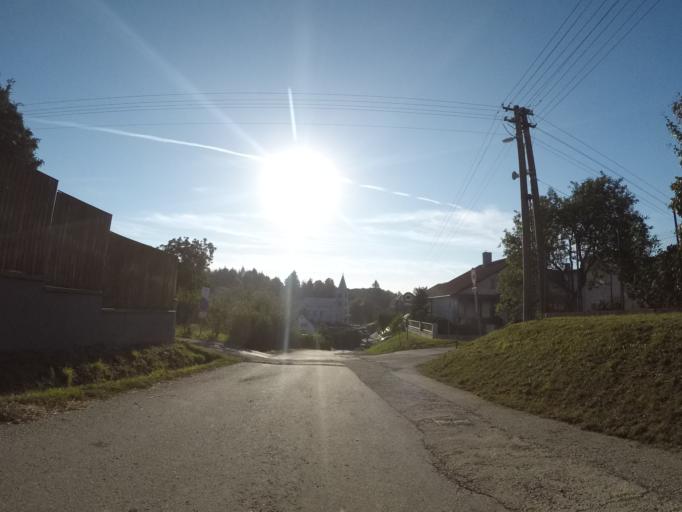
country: SK
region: Kosicky
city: Kosice
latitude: 48.7317
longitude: 21.1405
